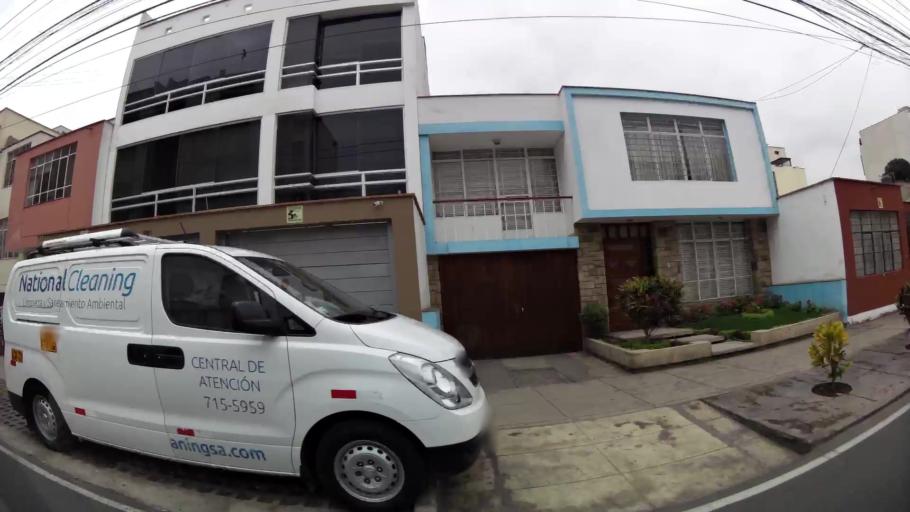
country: PE
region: Lima
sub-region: Lima
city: Surco
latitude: -12.1325
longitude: -77.0198
